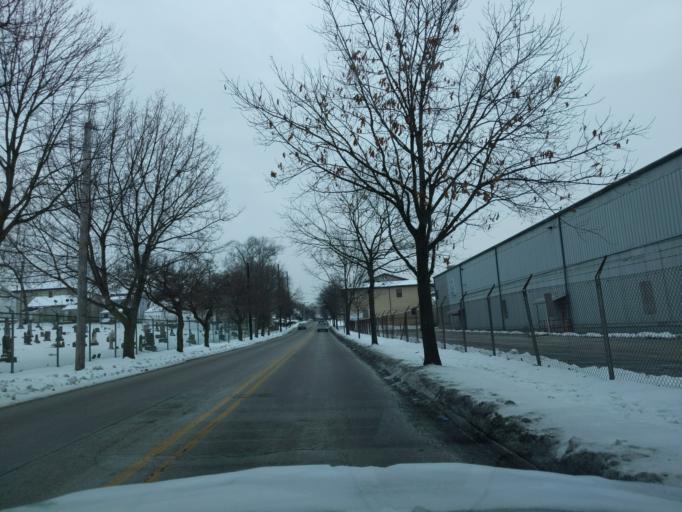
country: US
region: Indiana
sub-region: Tippecanoe County
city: Lafayette
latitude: 40.4311
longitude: -86.8873
